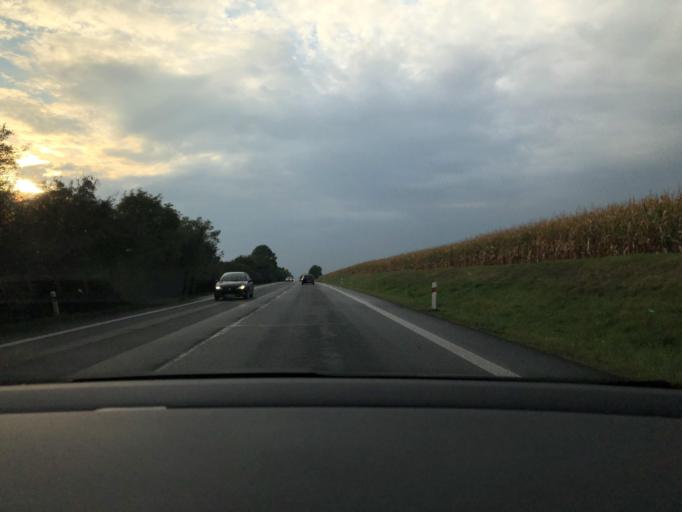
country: CZ
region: Central Bohemia
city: Velim
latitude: 50.0366
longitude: 15.1423
